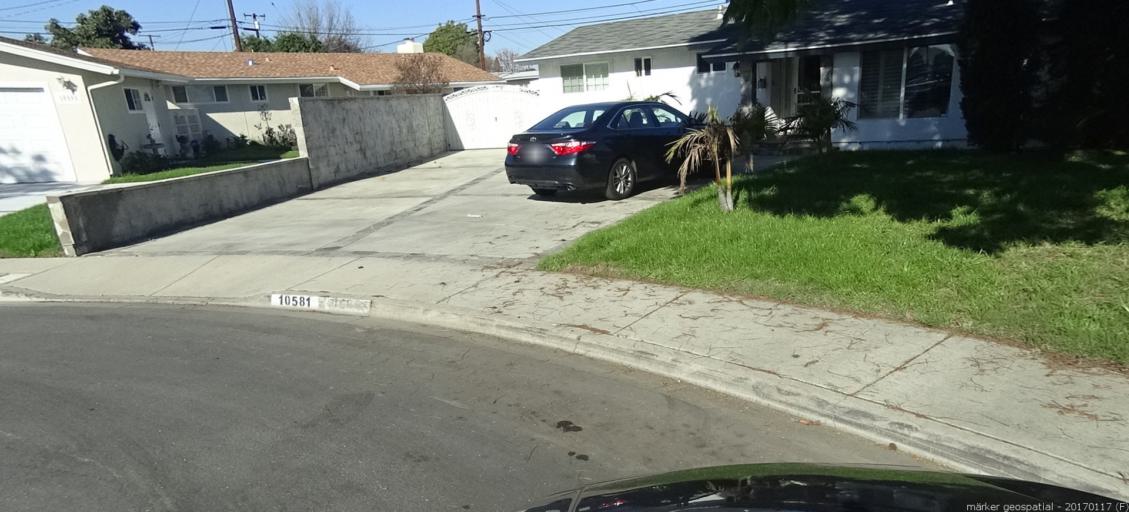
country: US
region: California
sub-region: Orange County
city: Stanton
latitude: 33.8089
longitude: -117.9657
